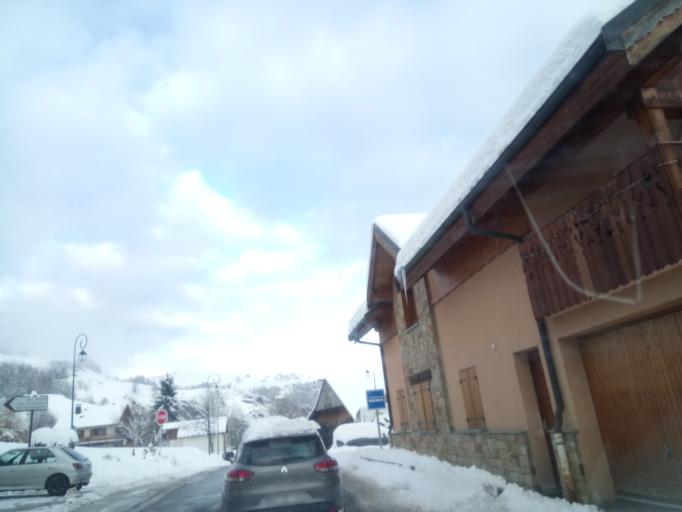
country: FR
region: Rhone-Alpes
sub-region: Departement de la Savoie
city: Saint-Jean-de-Maurienne
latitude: 45.2457
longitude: 6.2799
